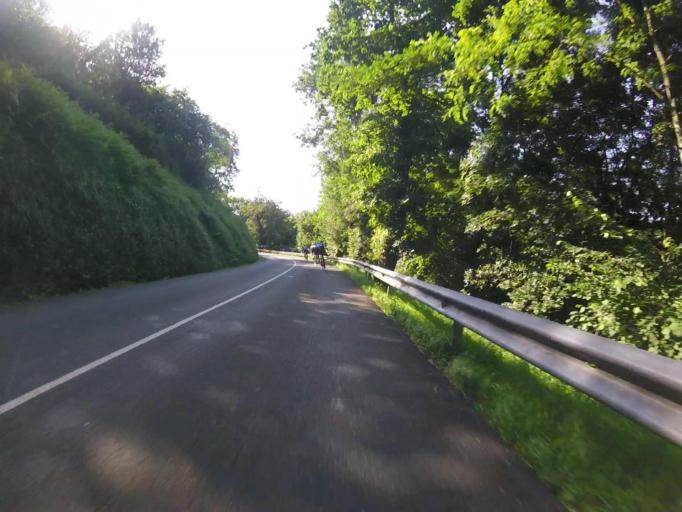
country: ES
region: Basque Country
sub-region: Provincia de Guipuzcoa
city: Asteasu
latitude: 43.2046
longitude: -2.1113
